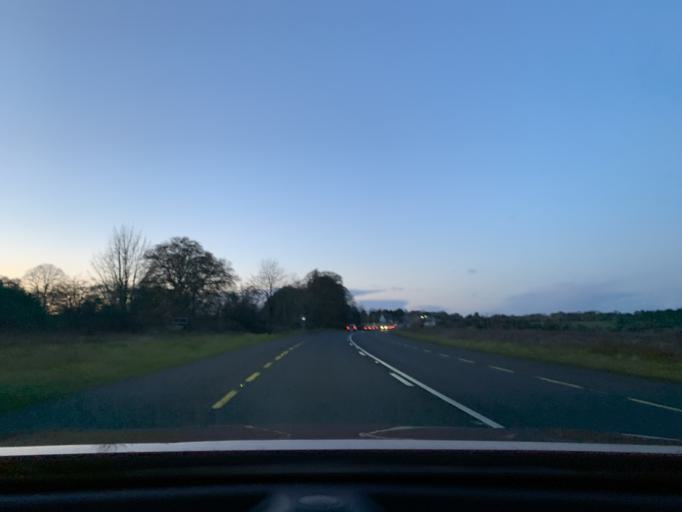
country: IE
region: Connaught
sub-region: County Leitrim
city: Carrick-on-Shannon
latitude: 53.9619
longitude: -8.1925
